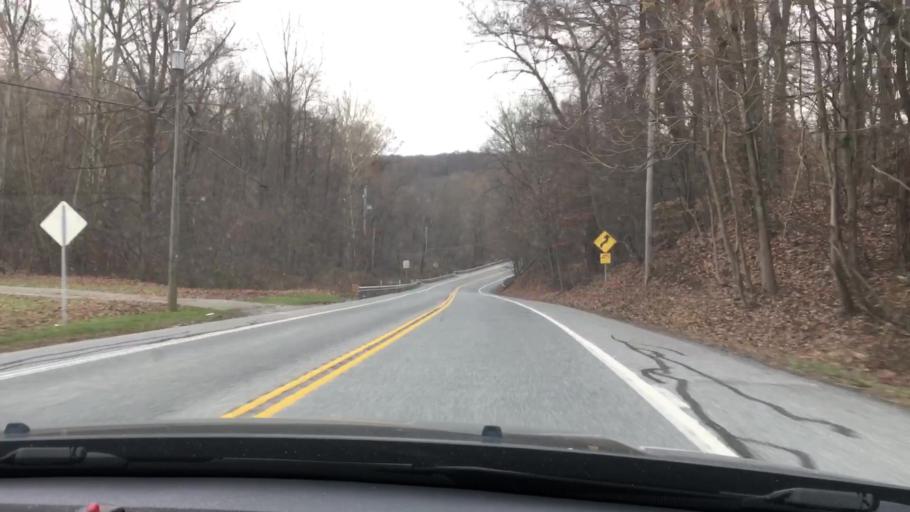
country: US
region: Pennsylvania
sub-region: Lancaster County
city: Willow Street
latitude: 39.9150
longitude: -76.2446
